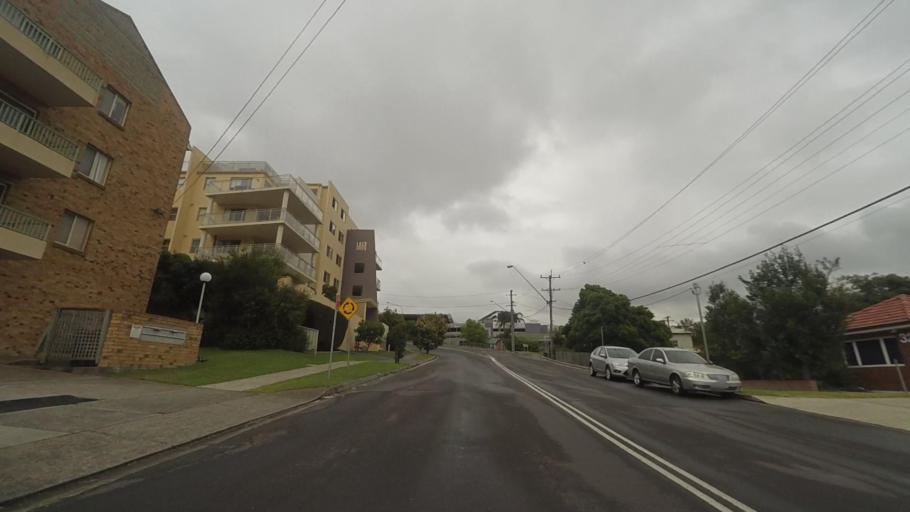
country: AU
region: New South Wales
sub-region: Wollongong
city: Gwynneville
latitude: -34.4227
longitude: 150.8826
